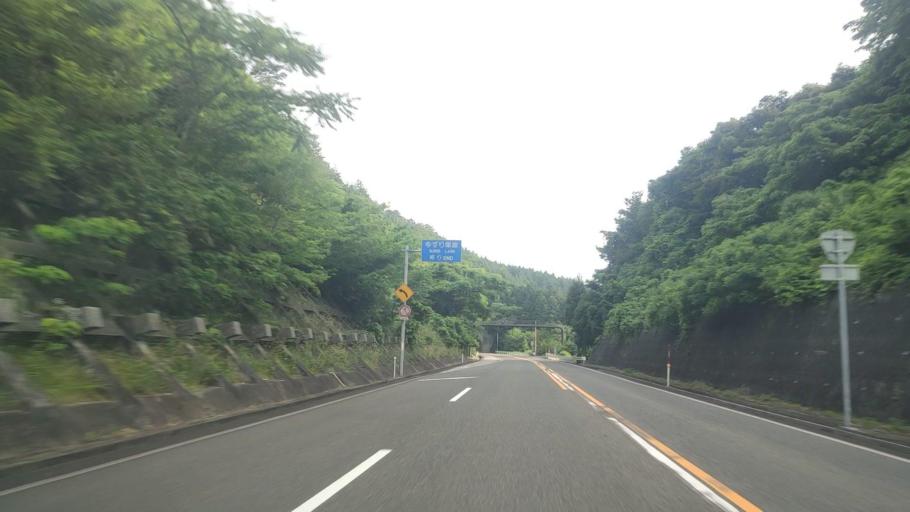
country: JP
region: Tottori
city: Kurayoshi
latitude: 35.3472
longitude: 133.7493
